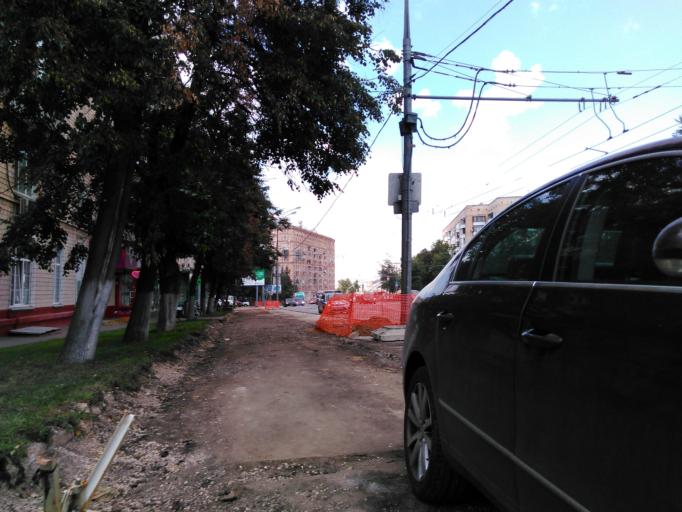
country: RU
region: Moscow
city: Novyye Cheremushki
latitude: 55.6975
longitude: 37.6202
